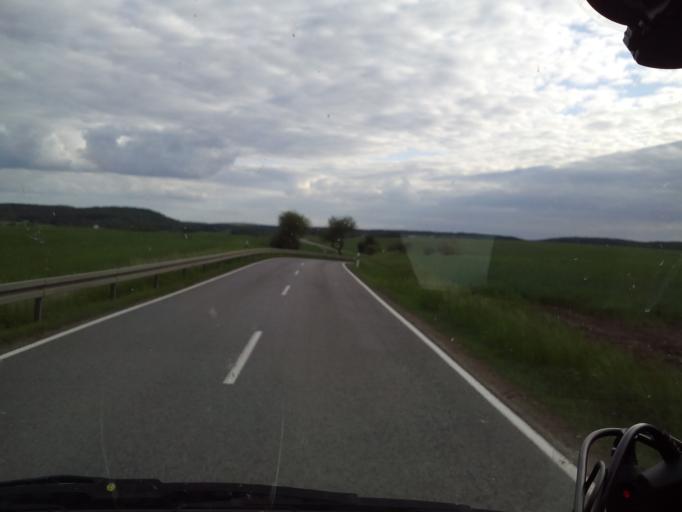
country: DE
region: Thuringia
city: Hellingen
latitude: 50.2633
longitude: 10.6937
